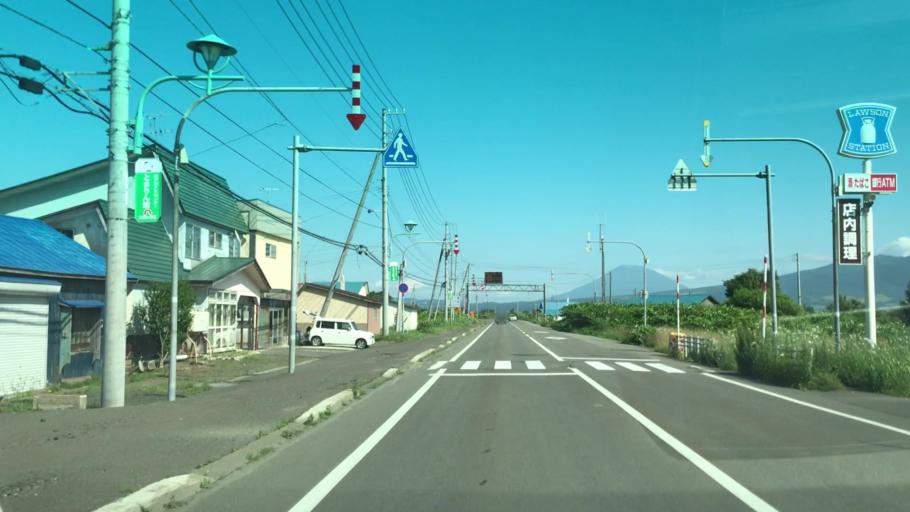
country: JP
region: Hokkaido
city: Iwanai
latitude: 43.0308
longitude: 140.5376
